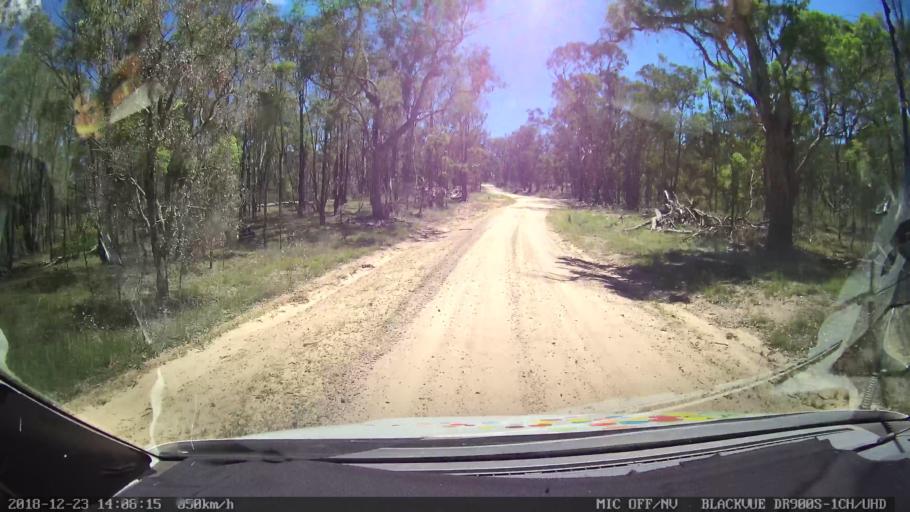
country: AU
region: New South Wales
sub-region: Tamworth Municipality
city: Manilla
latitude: -30.6411
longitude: 151.0690
